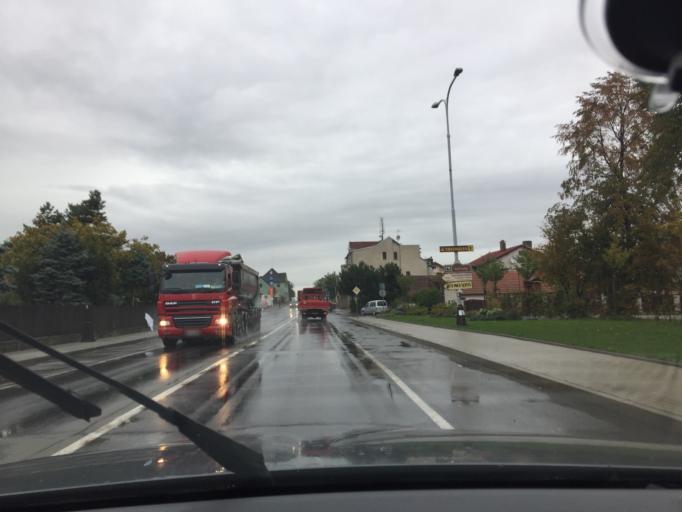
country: CZ
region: Central Bohemia
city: Klecany
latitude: 50.2014
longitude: 14.4348
